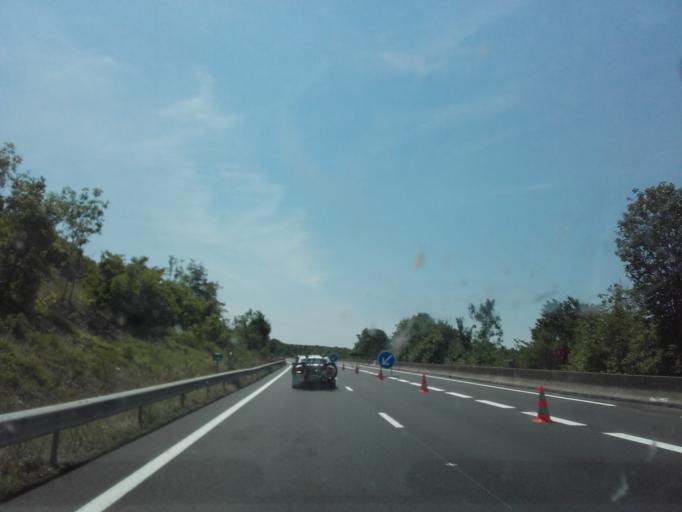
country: FR
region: Bourgogne
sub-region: Departement de la Cote-d'Or
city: Savigny-les-Beaune
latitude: 47.1285
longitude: 4.6992
